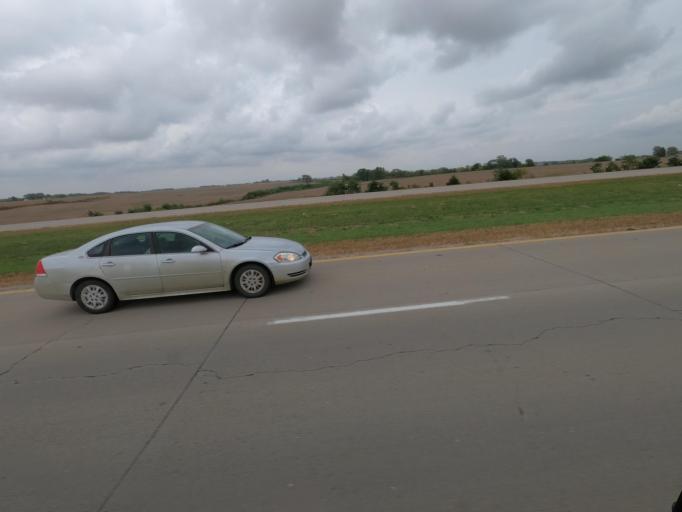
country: US
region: Iowa
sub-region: Wapello County
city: Ottumwa
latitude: 41.0004
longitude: -92.2441
